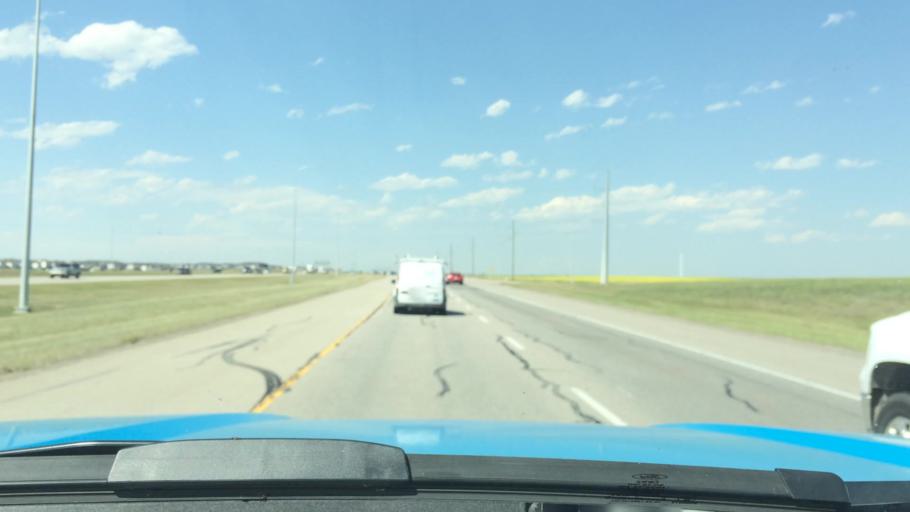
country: CA
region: Alberta
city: Chestermere
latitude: 51.0985
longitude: -113.9183
